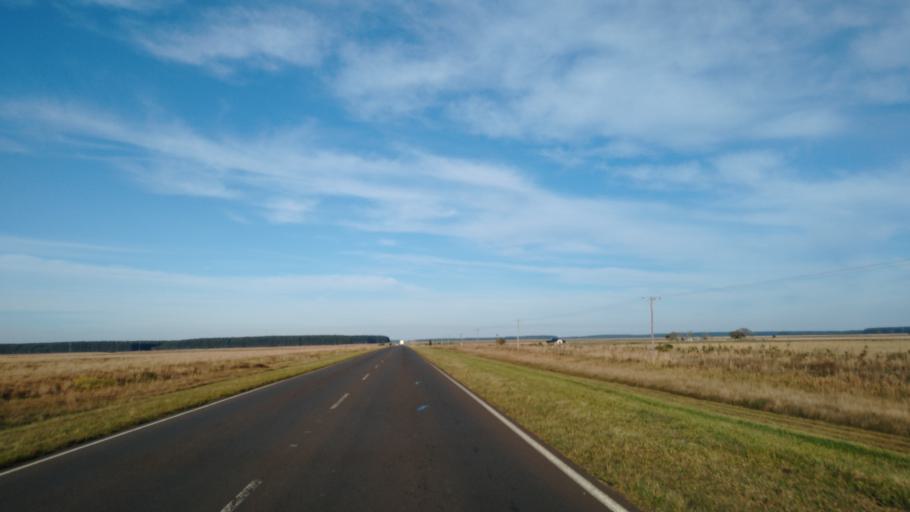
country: AR
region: Corrientes
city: La Cruz
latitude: -29.2928
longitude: -56.7688
